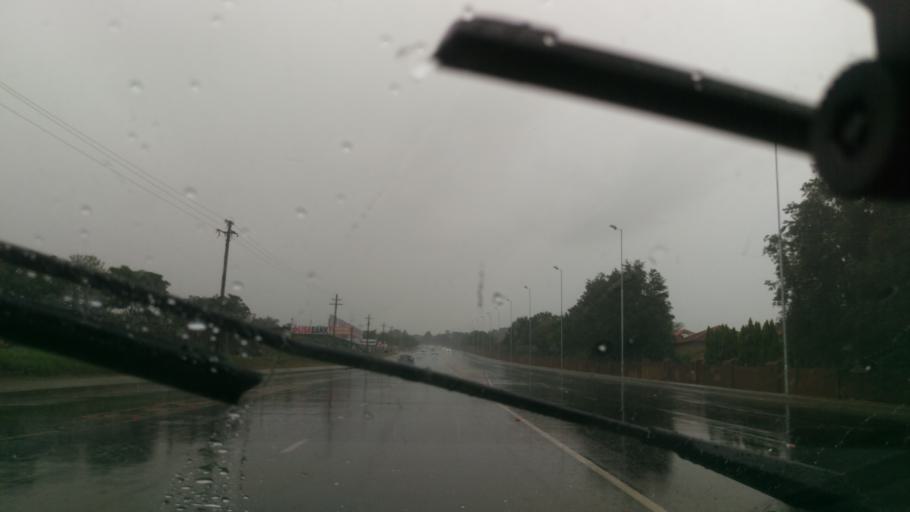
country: ZA
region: Gauteng
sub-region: City of Johannesburg Metropolitan Municipality
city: Diepsloot
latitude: -26.0035
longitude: 27.9873
